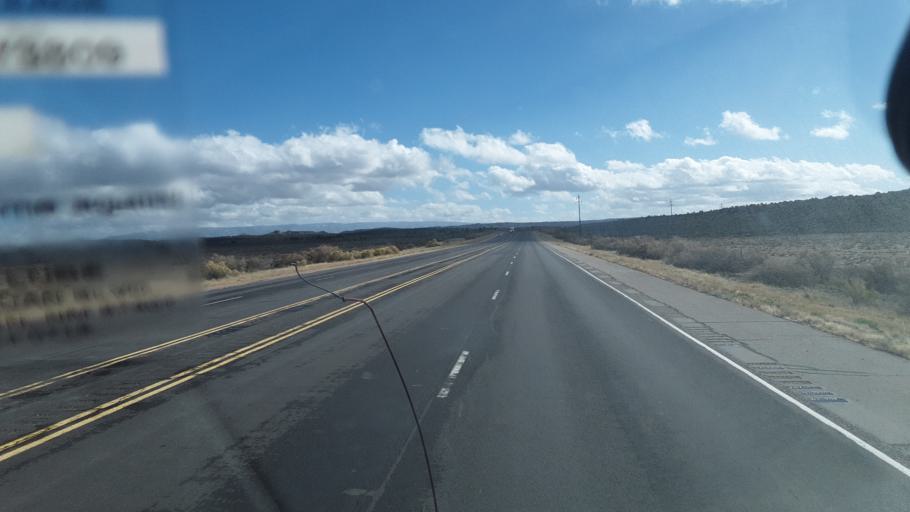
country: US
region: New Mexico
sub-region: Rio Arriba County
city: Santa Teresa
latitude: 36.1304
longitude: -107.2122
